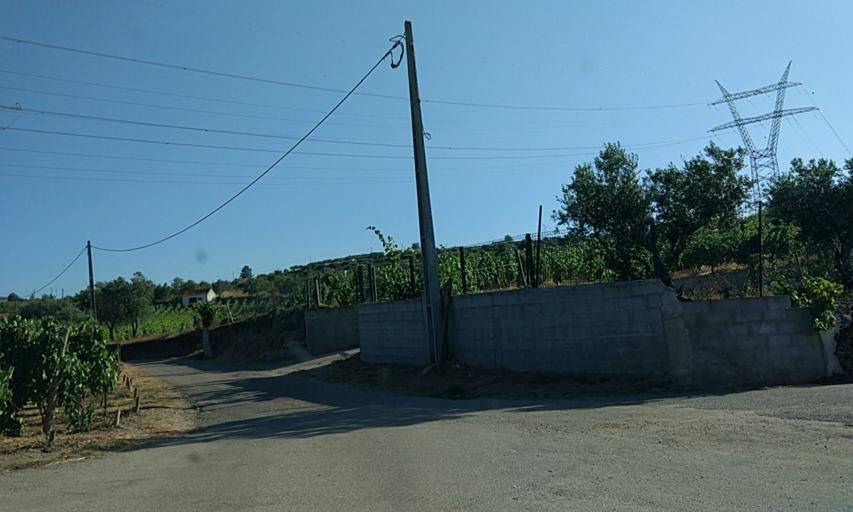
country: PT
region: Viseu
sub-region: Sao Joao da Pesqueira
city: Sao Joao da Pesqueira
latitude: 41.1571
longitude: -7.4197
